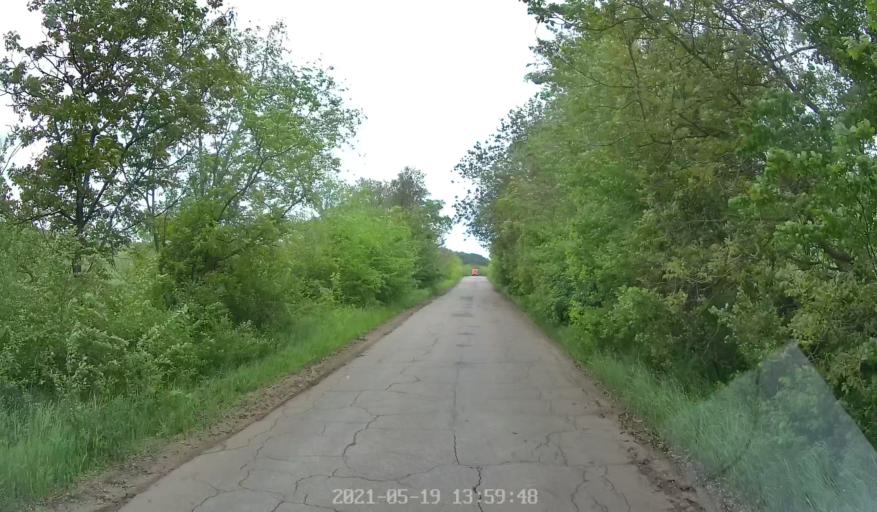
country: MD
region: Chisinau
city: Chisinau
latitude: 47.0384
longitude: 28.9267
